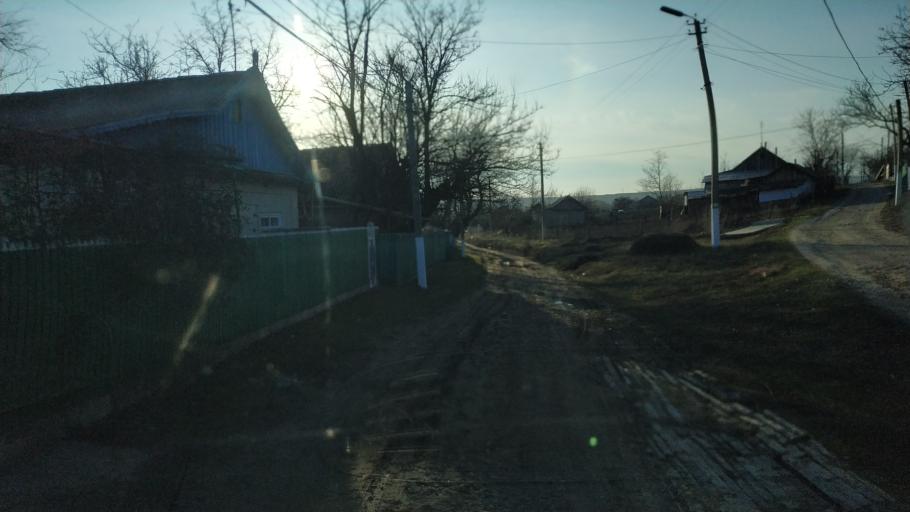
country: MD
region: Hincesti
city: Hincesti
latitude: 46.6999
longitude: 28.5324
